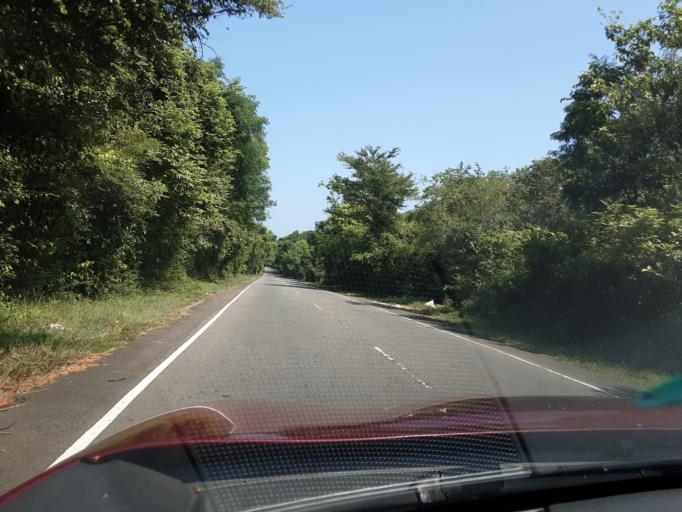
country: LK
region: Uva
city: Badulla
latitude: 7.2664
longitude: 81.0516
